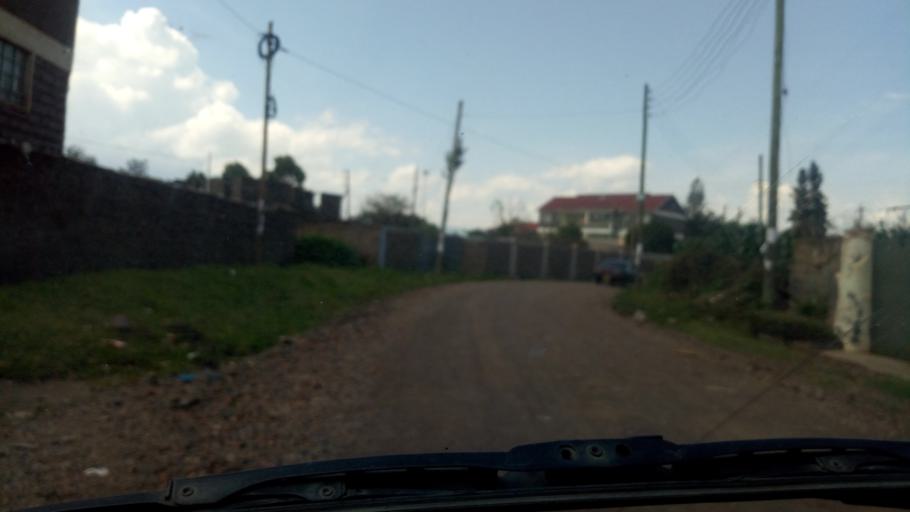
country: KE
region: Nakuru
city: Nakuru
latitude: -0.2770
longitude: 36.1046
